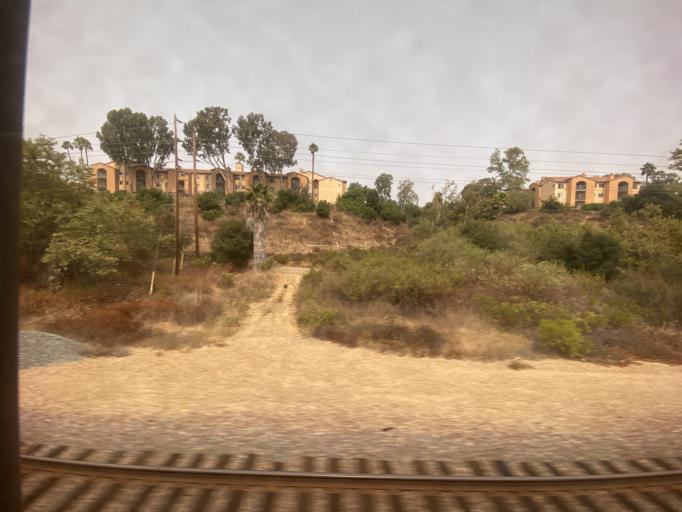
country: US
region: California
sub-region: San Diego County
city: La Jolla
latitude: 32.8625
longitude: -117.1971
